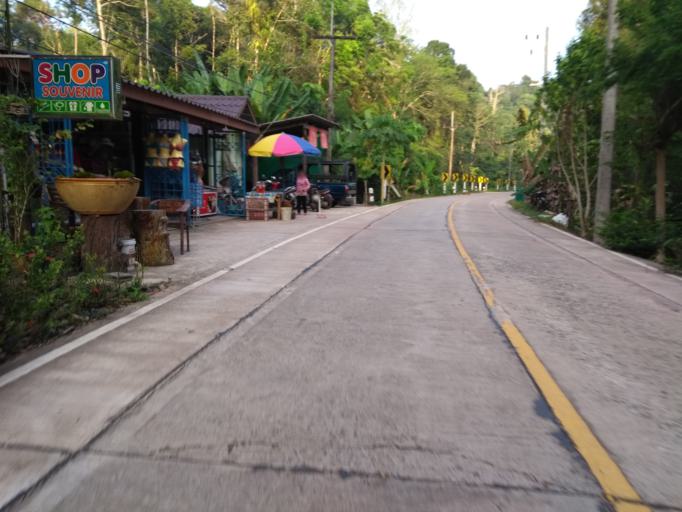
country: TH
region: Trat
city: Ko Kut
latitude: 11.6016
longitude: 102.5693
